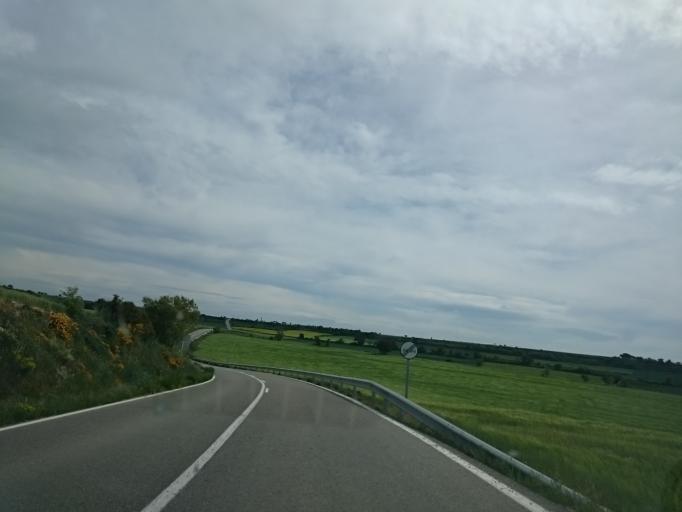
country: ES
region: Catalonia
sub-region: Provincia de Lleida
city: Ivorra
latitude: 41.7602
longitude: 1.3803
